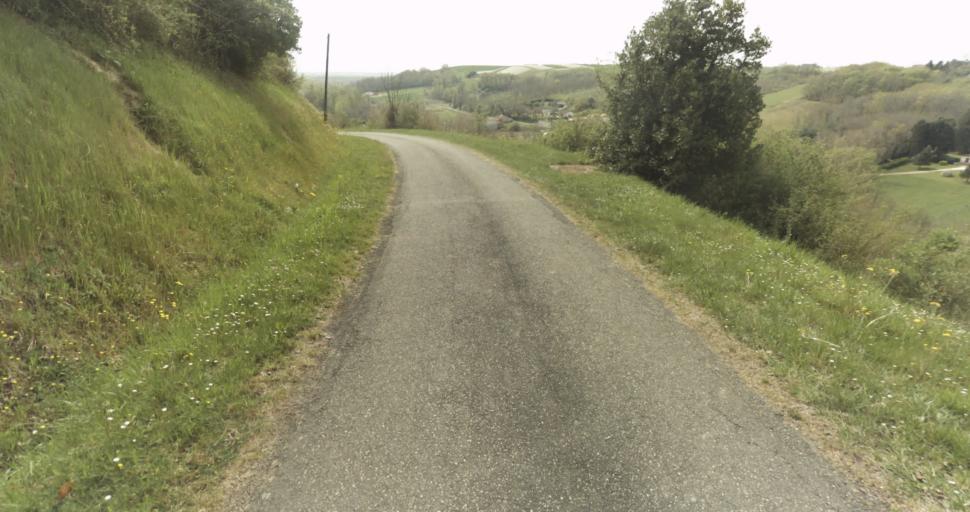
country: FR
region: Midi-Pyrenees
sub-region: Departement du Tarn-et-Garonne
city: Moissac
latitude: 44.1097
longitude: 1.0537
